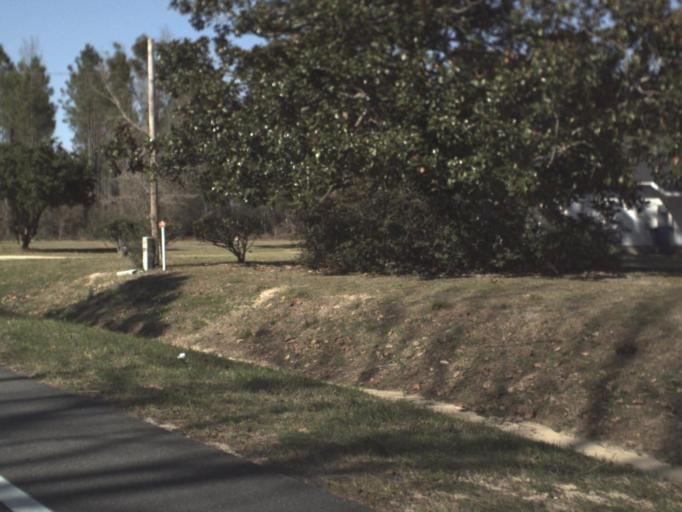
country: US
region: Florida
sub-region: Gulf County
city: Wewahitchka
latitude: 30.2519
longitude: -85.2303
